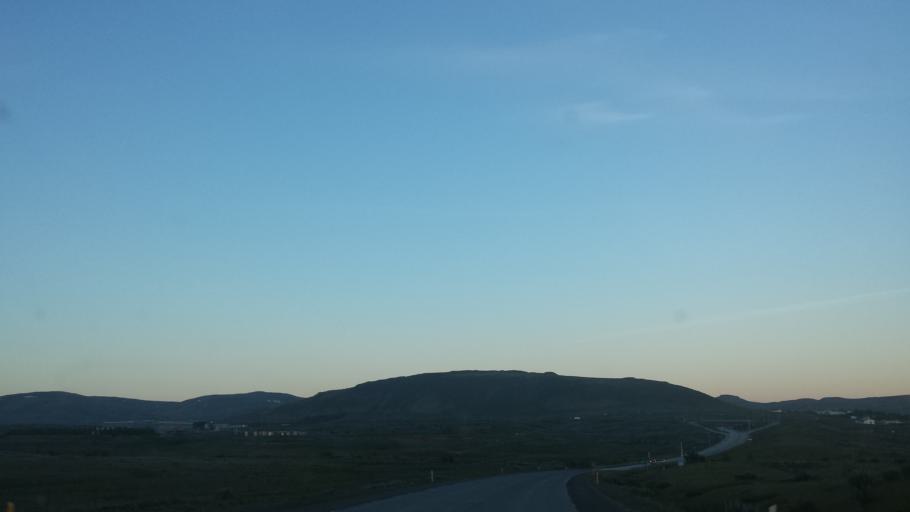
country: IS
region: Capital Region
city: Mosfellsbaer
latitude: 64.1912
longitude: -21.6900
